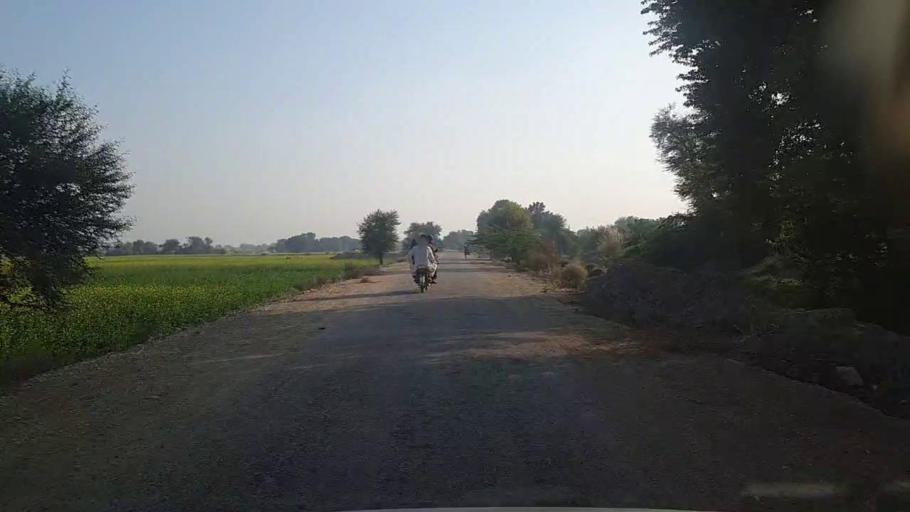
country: PK
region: Sindh
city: Karaundi
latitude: 26.7497
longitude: 68.4765
